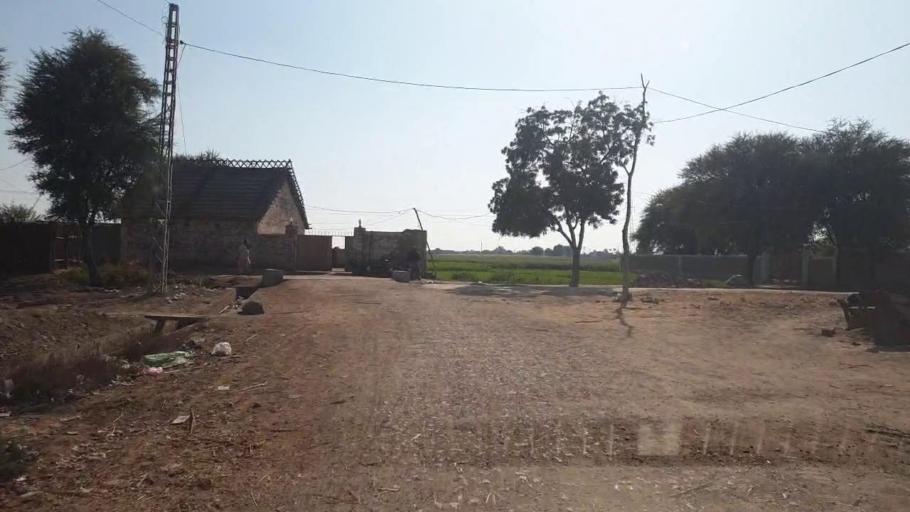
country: PK
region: Sindh
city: Shahpur Chakar
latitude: 26.1459
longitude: 68.6759
